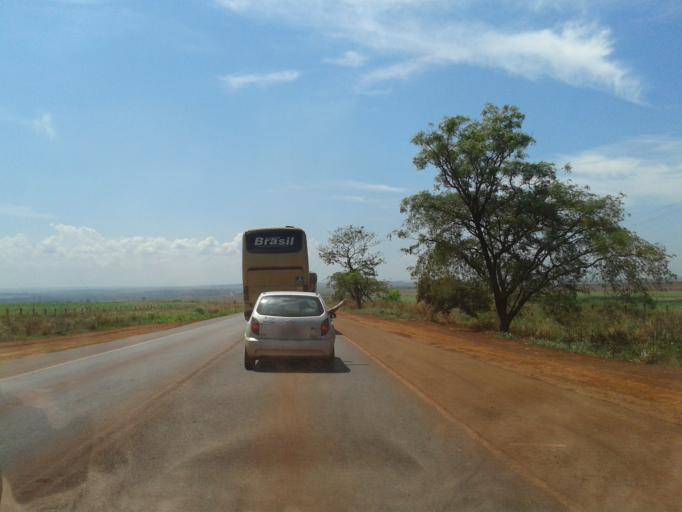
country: BR
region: Goias
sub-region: Santa Helena De Goias
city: Santa Helena de Goias
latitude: -18.0213
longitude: -50.3349
